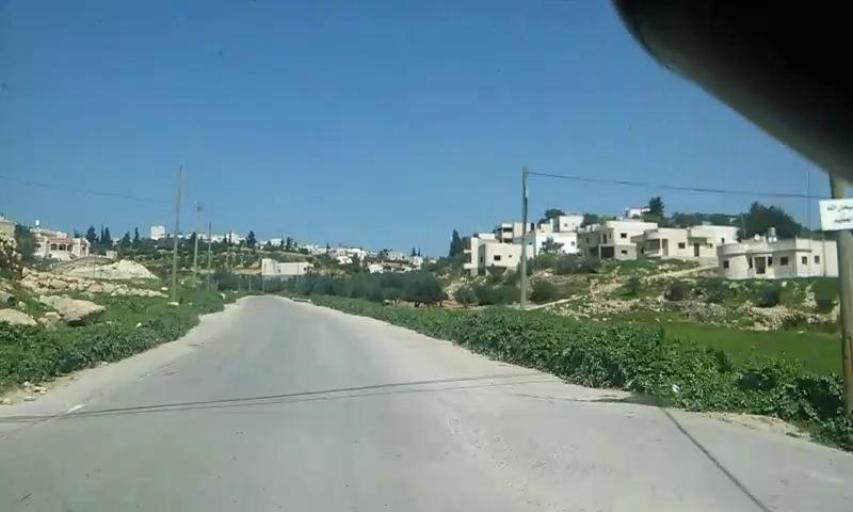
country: PS
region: West Bank
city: Idhna
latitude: 31.5513
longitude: 34.9691
